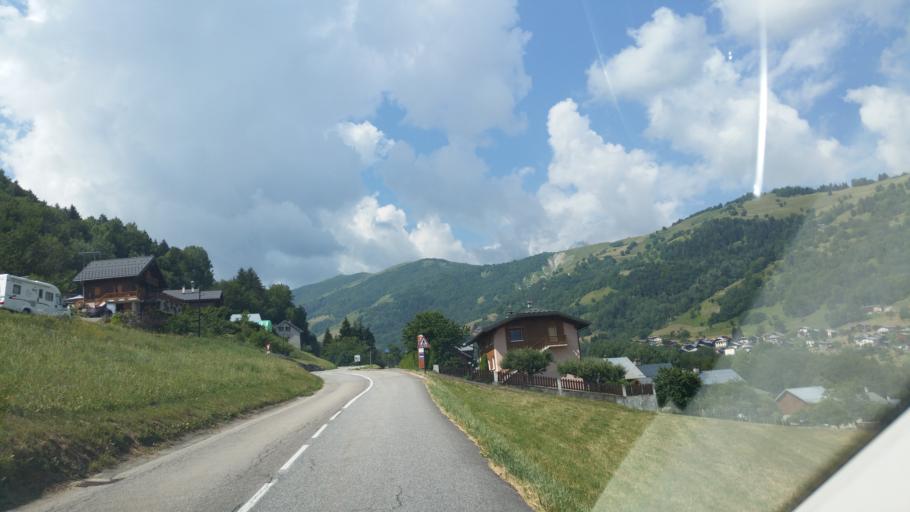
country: FR
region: Rhone-Alpes
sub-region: Departement de la Savoie
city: Aigueblanche
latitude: 45.4880
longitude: 6.4675
